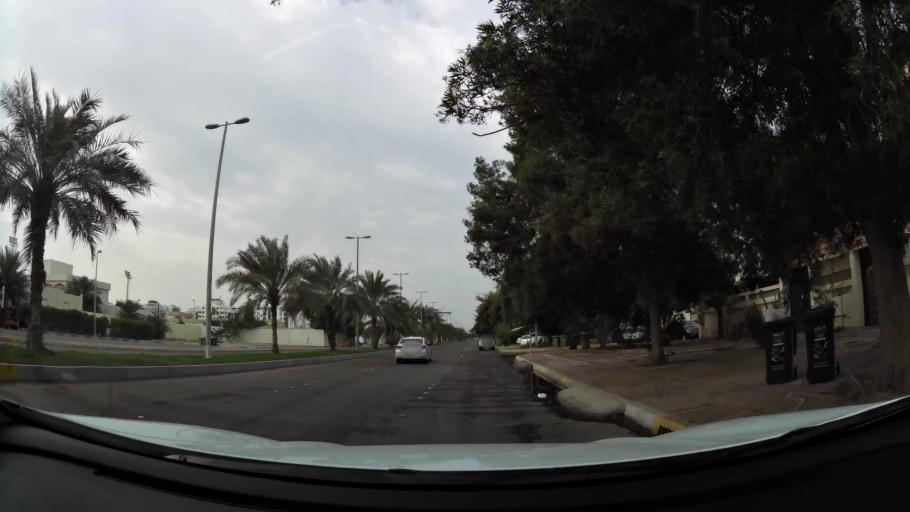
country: AE
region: Abu Dhabi
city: Abu Dhabi
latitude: 24.4520
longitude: 54.4019
